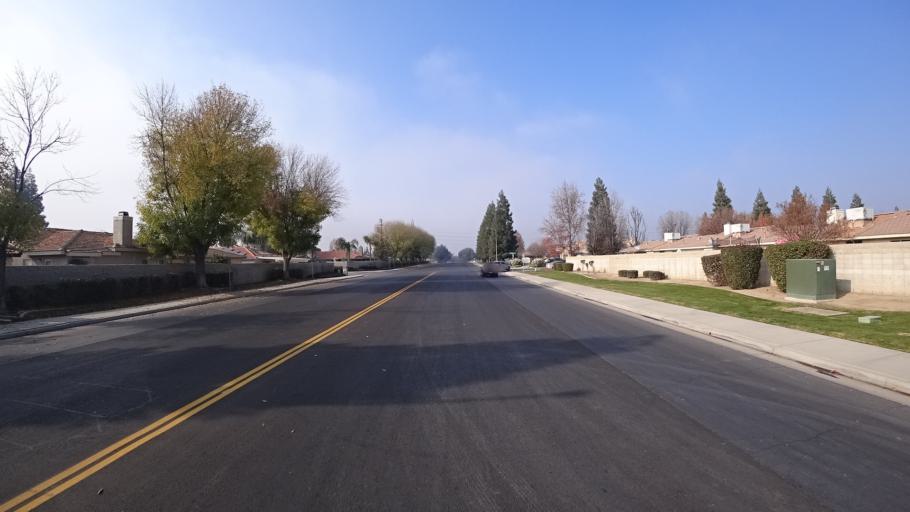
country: US
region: California
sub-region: Kern County
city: Greenacres
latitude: 35.3253
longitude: -119.0932
